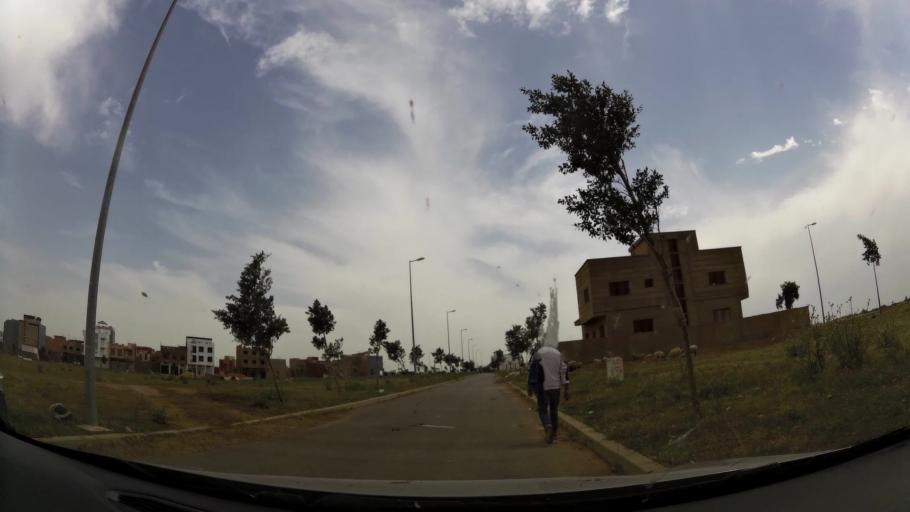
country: MA
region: Rabat-Sale-Zemmour-Zaer
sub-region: Khemisset
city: Khemisset
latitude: 33.8139
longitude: -6.0923
